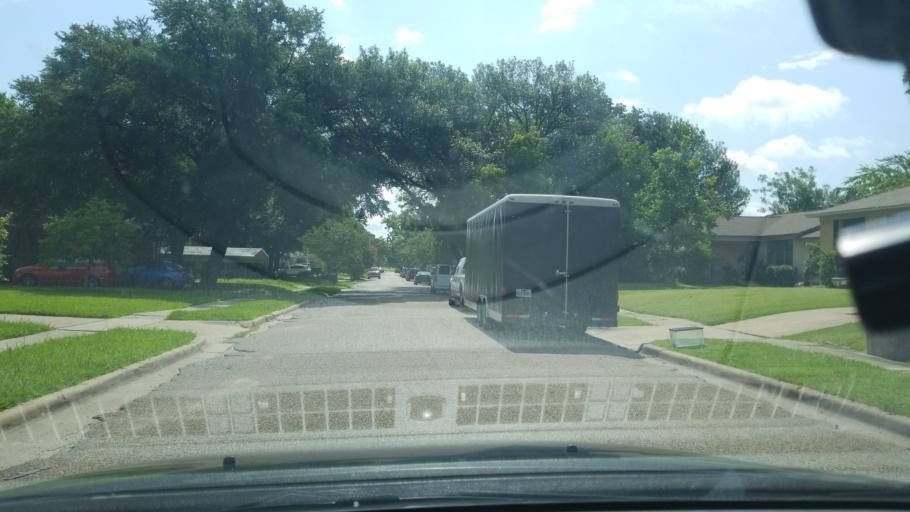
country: US
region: Texas
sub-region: Dallas County
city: Mesquite
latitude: 32.8156
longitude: -96.6531
